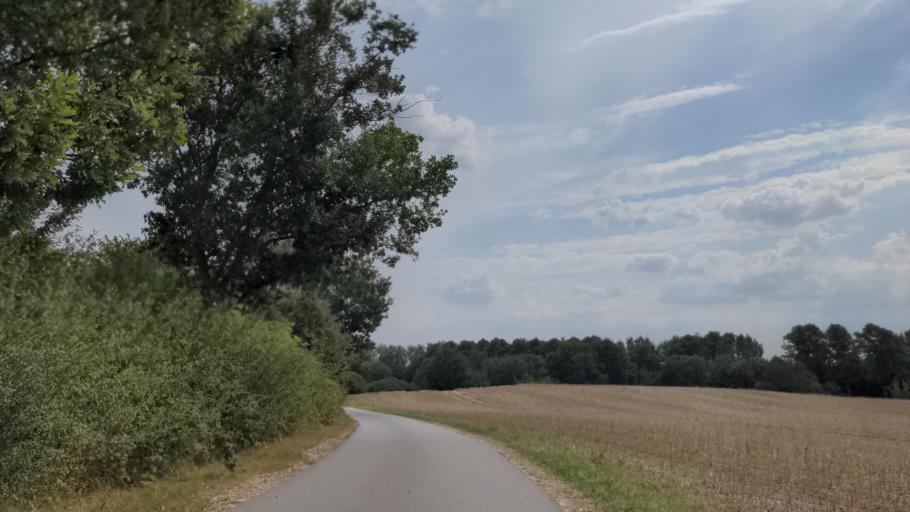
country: DE
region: Mecklenburg-Vorpommern
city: Selmsdorf
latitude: 53.8717
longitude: 10.8961
